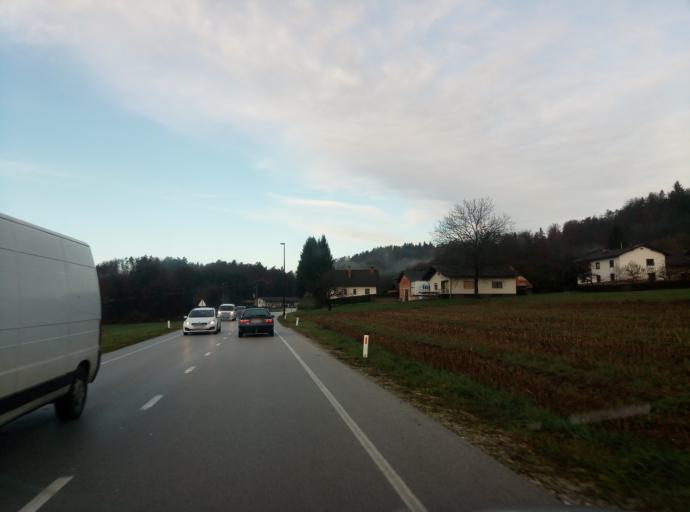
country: SI
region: Komenda
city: Moste
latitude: 46.1687
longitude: 14.5331
